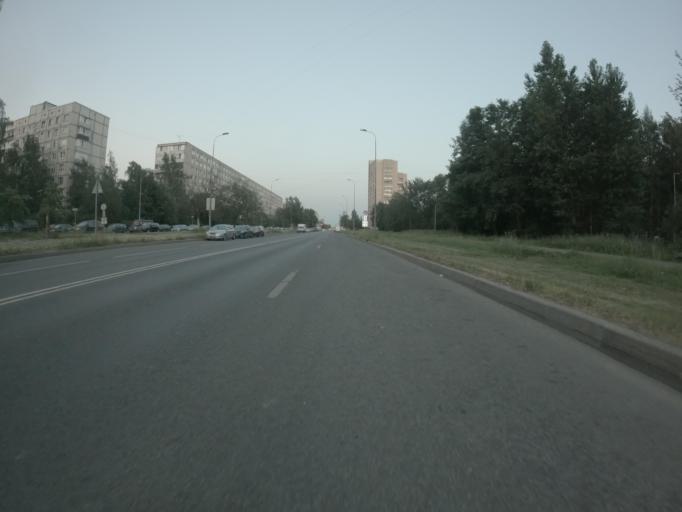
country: RU
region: St.-Petersburg
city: Krasnogvargeisky
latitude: 59.9178
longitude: 30.4825
